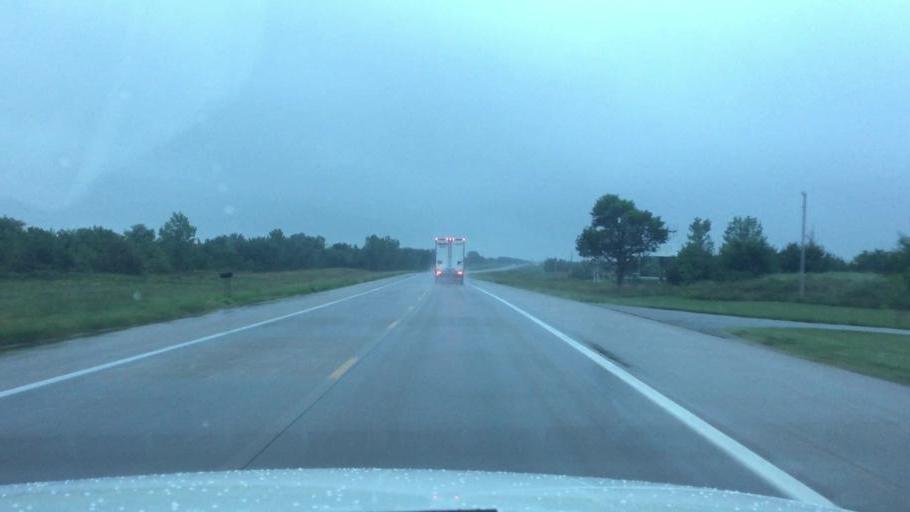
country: US
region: Kansas
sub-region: Neosho County
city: Chanute
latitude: 37.5246
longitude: -95.4714
